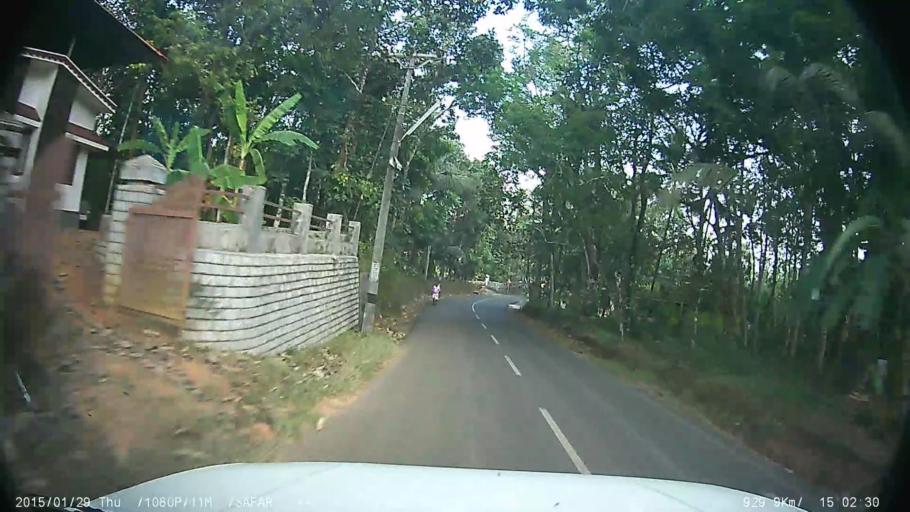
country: IN
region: Kerala
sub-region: Kottayam
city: Palackattumala
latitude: 9.7267
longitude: 76.5759
